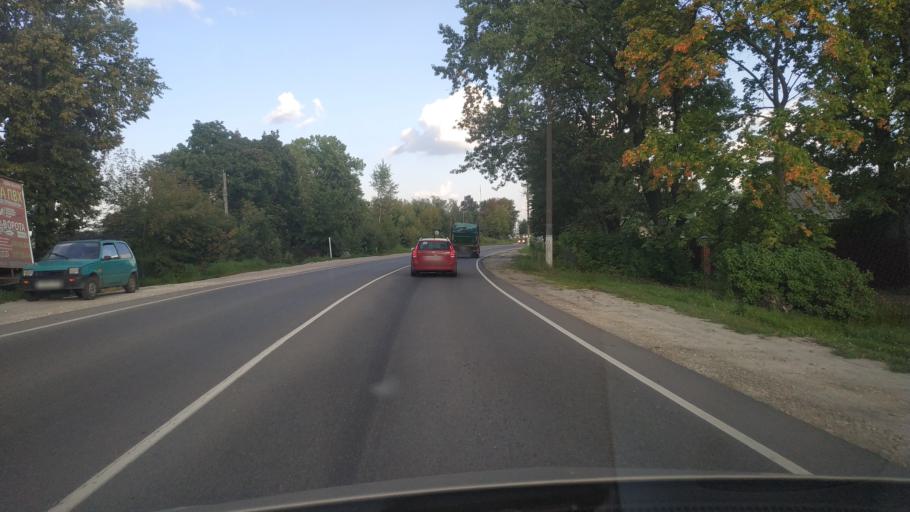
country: RU
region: Moskovskaya
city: Shatura
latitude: 55.5790
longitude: 39.4836
